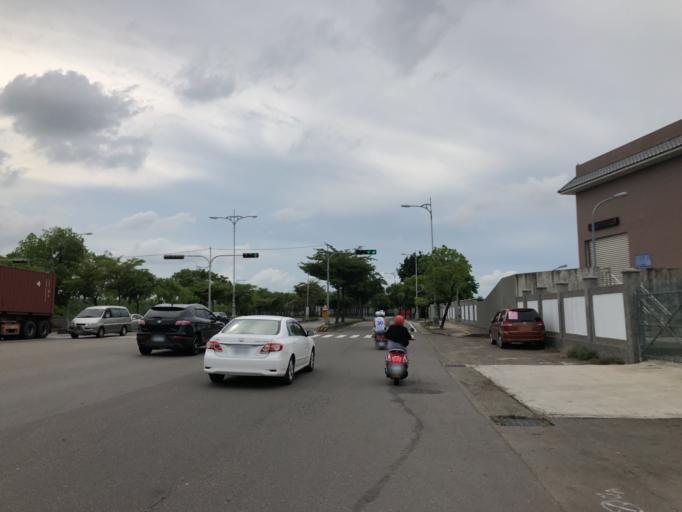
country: TW
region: Taiwan
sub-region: Taichung City
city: Taichung
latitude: 24.0899
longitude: 120.6535
